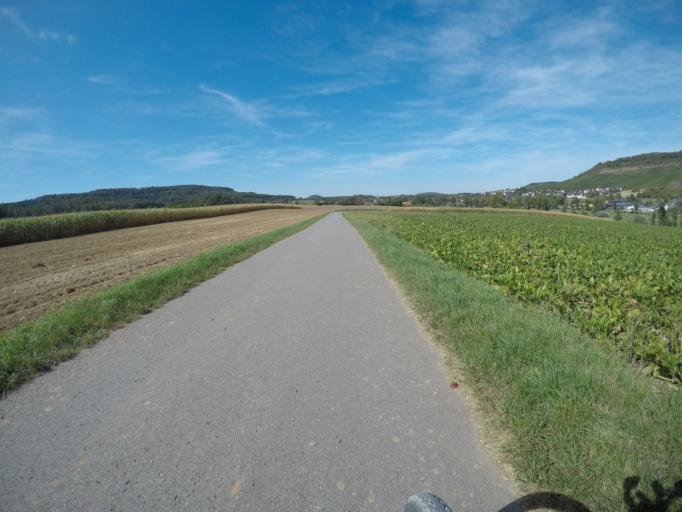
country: DE
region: Baden-Wuerttemberg
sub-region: Karlsruhe Region
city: Illingen
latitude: 48.9908
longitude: 8.9112
